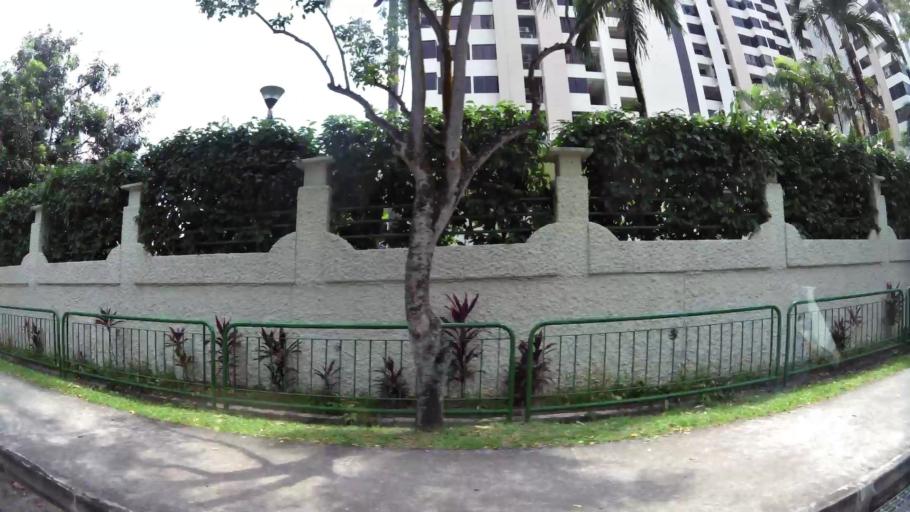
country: SG
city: Singapore
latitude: 1.3003
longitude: 103.8877
